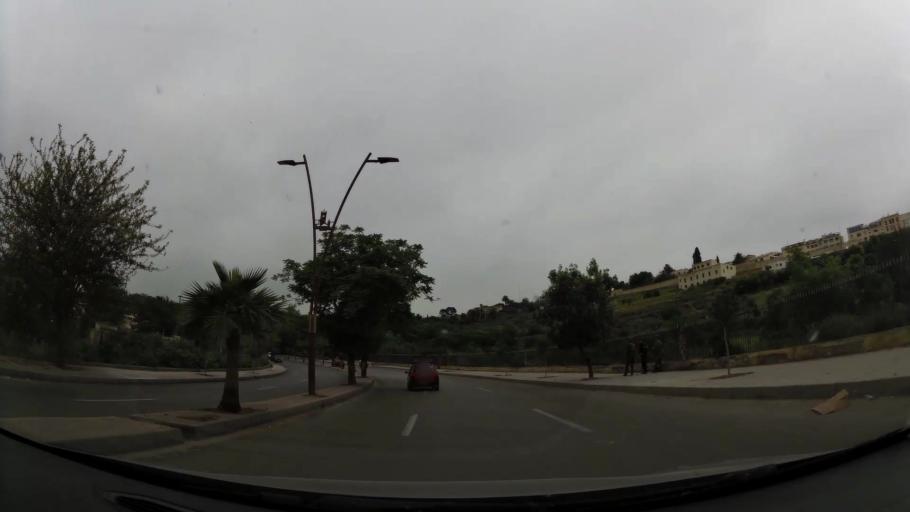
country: MA
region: Fes-Boulemane
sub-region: Fes
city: Fes
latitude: 34.0550
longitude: -4.9760
